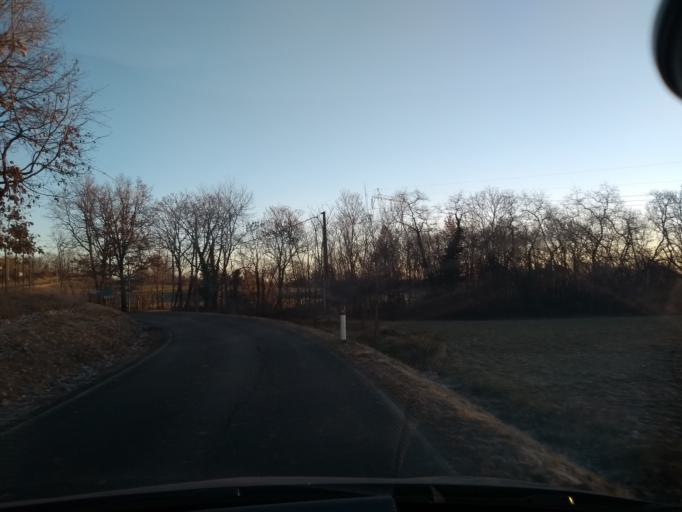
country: IT
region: Piedmont
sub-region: Provincia di Torino
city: Balangero
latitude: 45.2773
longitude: 7.5385
